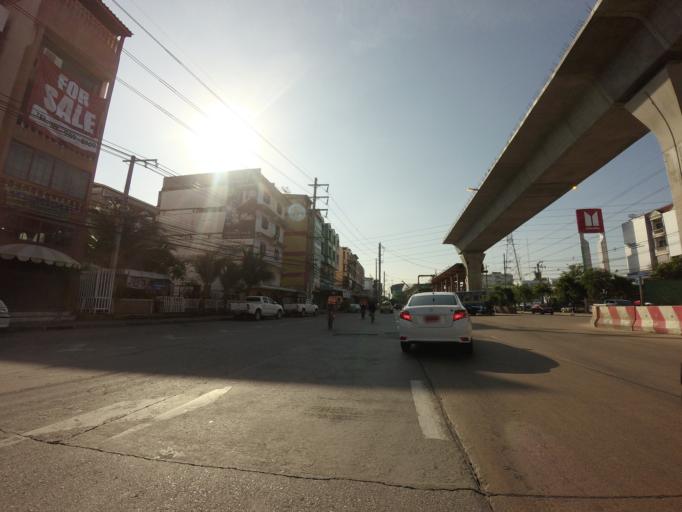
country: TH
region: Samut Prakan
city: Samut Prakan
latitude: 13.6244
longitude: 100.5892
